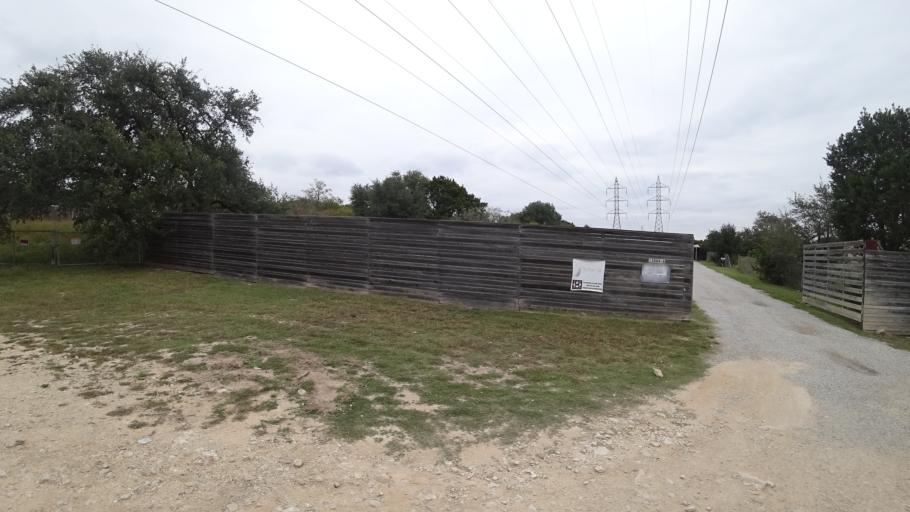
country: US
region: Texas
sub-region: Travis County
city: Hudson Bend
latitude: 30.3806
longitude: -97.9362
